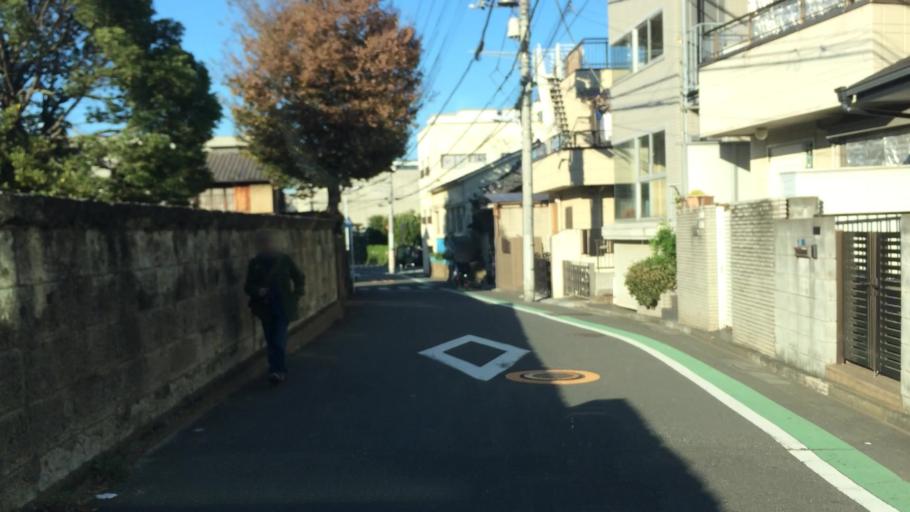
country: JP
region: Tokyo
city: Tokyo
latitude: 35.7245
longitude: 139.7659
